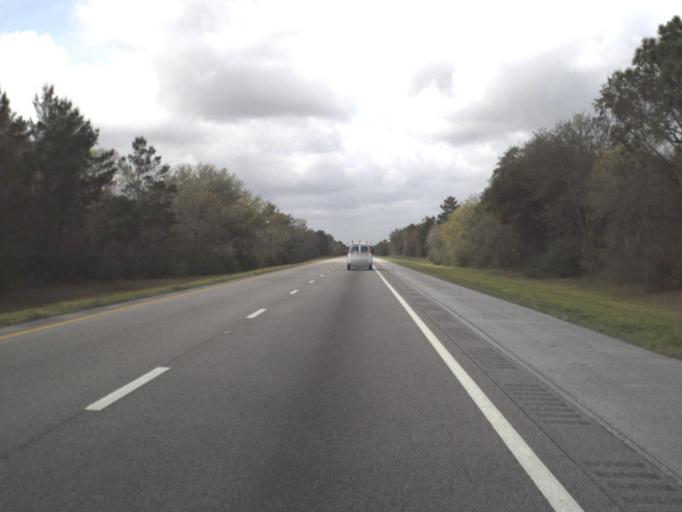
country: US
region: Florida
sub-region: Okaloosa County
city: Crestview
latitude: 30.7232
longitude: -86.4189
